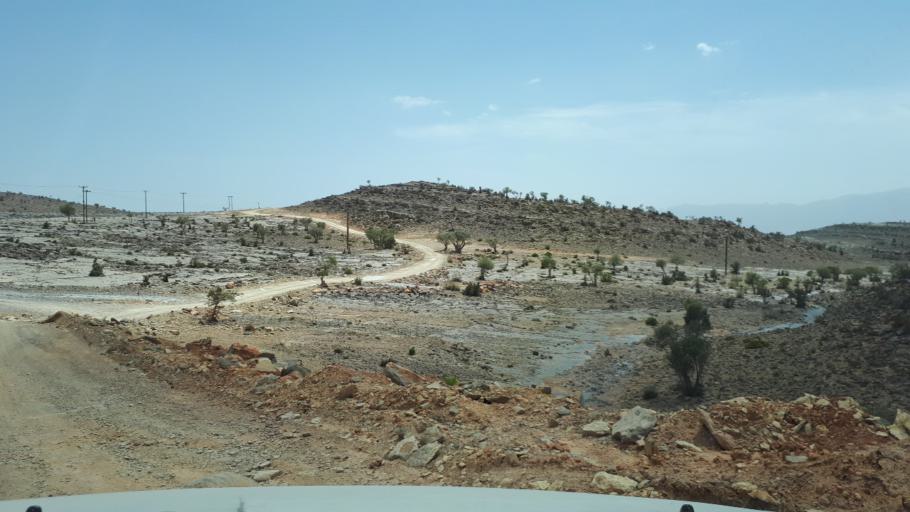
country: OM
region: Muhafazat ad Dakhiliyah
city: Bahla'
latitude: 23.2051
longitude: 57.2015
